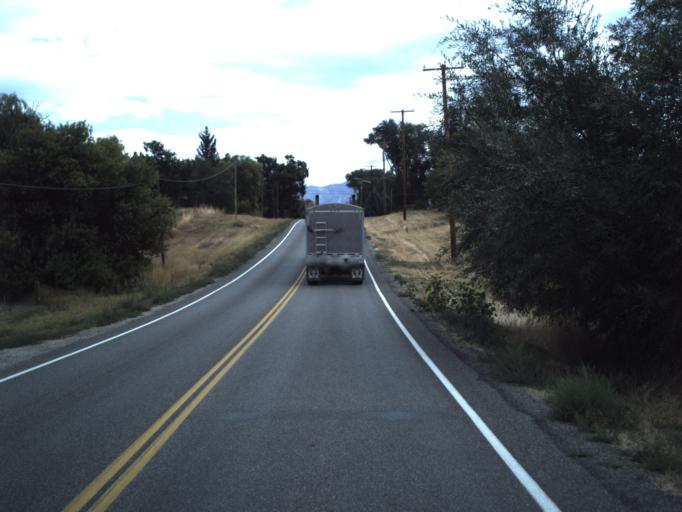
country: US
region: Utah
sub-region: Cache County
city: Benson
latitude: 41.8625
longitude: -111.9964
